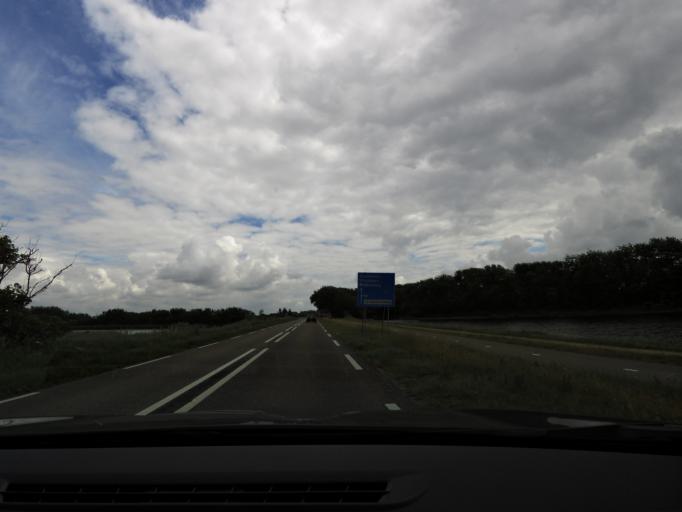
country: NL
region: Zeeland
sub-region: Gemeente Vlissingen
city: Vlissingen
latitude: 51.5207
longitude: 3.4544
